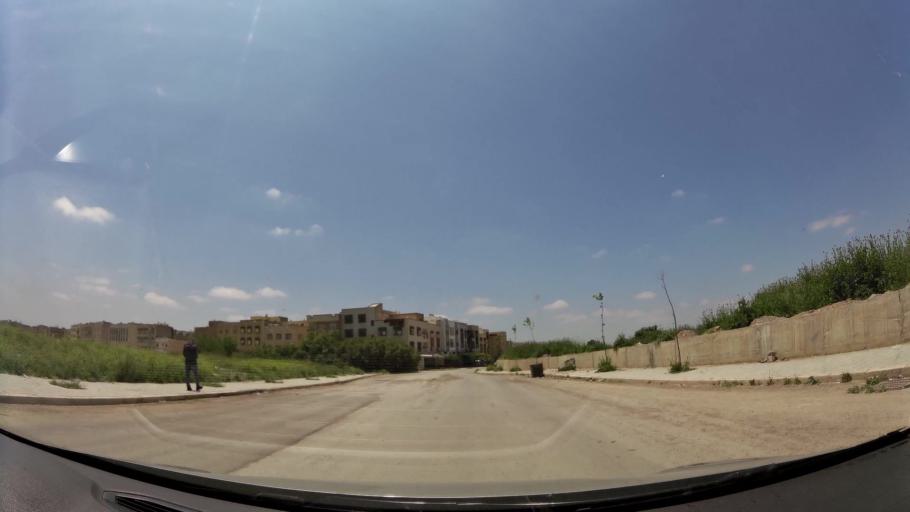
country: MA
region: Fes-Boulemane
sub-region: Fes
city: Fes
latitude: 34.0430
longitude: -5.0507
